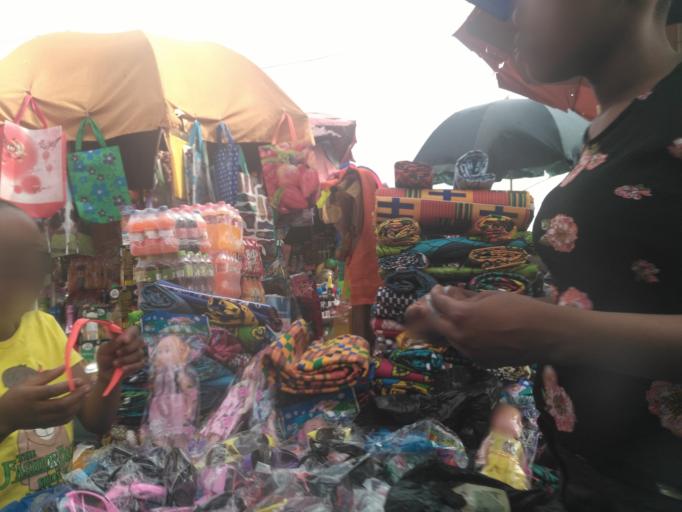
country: GH
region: Ashanti
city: Kumasi
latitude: 6.6988
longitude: -1.6205
